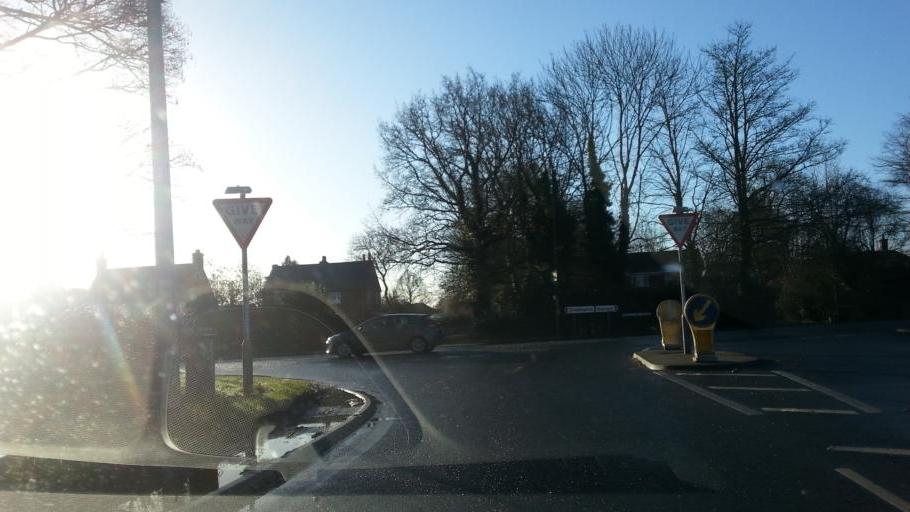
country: GB
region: England
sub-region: Nottinghamshire
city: Newark on Trent
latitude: 53.0778
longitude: -0.7747
